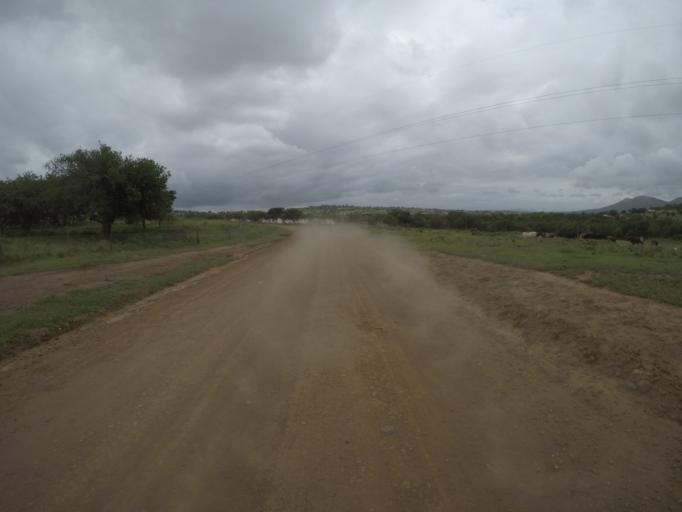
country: ZA
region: KwaZulu-Natal
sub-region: uThungulu District Municipality
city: Empangeni
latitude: -28.5933
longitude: 31.8408
